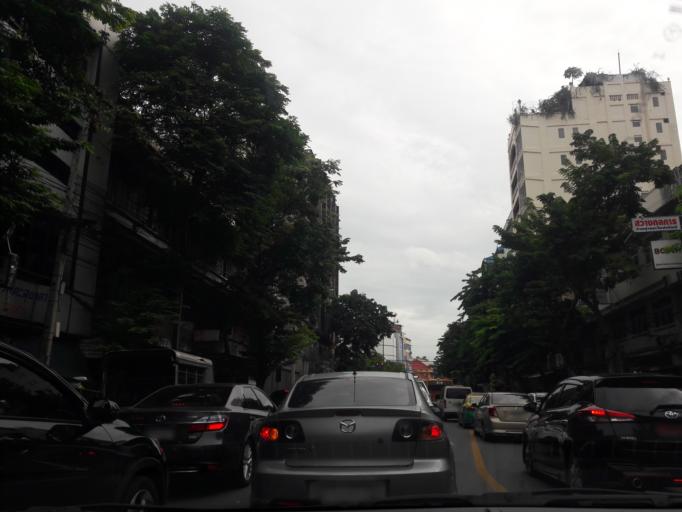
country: TH
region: Bangkok
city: Bangkok
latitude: 13.7478
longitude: 100.5069
